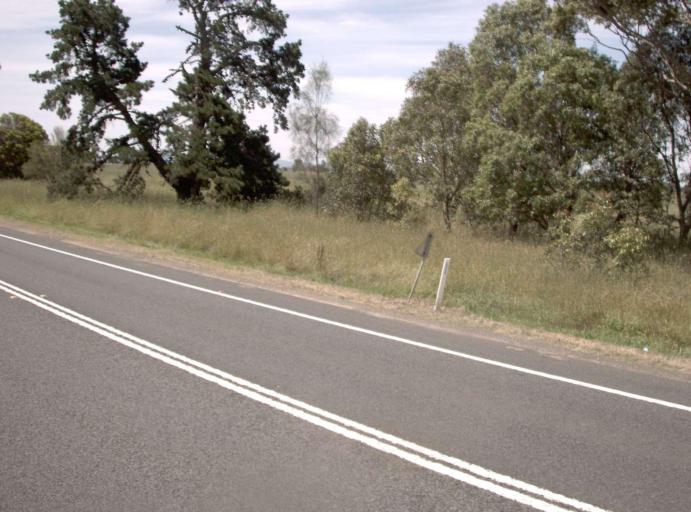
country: AU
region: Victoria
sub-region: Wellington
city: Sale
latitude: -38.0607
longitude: 147.0706
